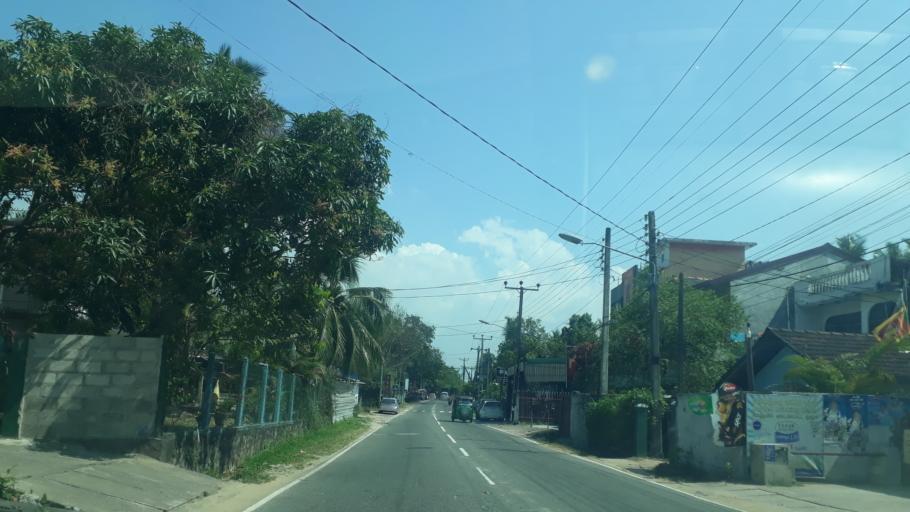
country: LK
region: Western
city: Gampaha
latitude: 7.0871
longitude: 80.0074
